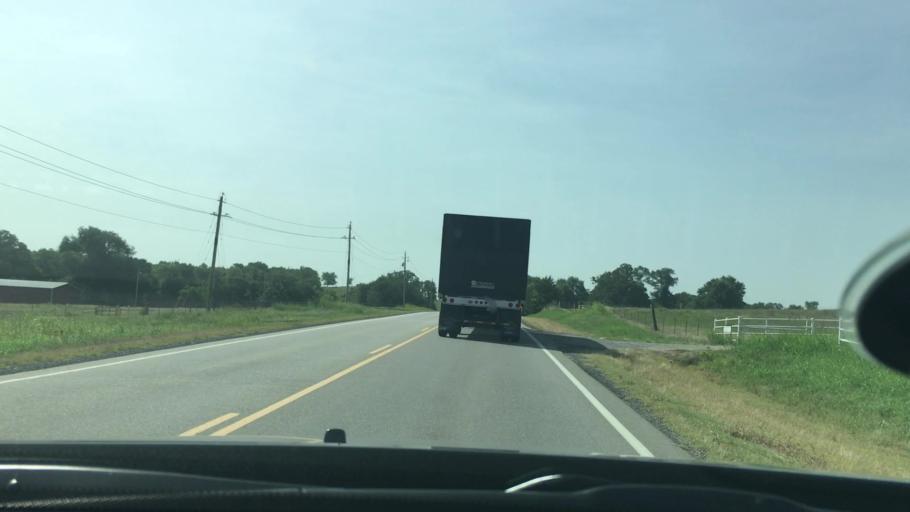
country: US
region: Oklahoma
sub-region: Atoka County
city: Atoka
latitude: 34.4080
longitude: -96.1812
